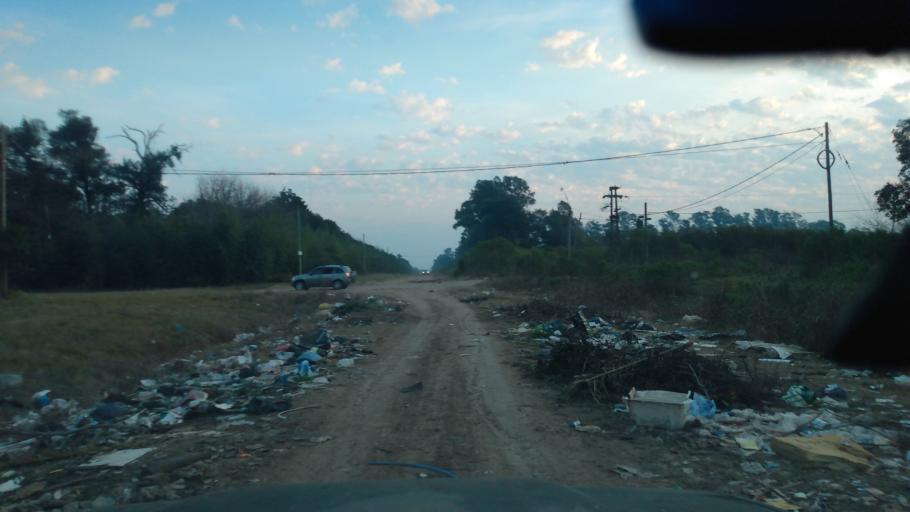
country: AR
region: Buenos Aires
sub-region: Partido de Lujan
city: Lujan
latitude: -34.5522
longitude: -59.1449
